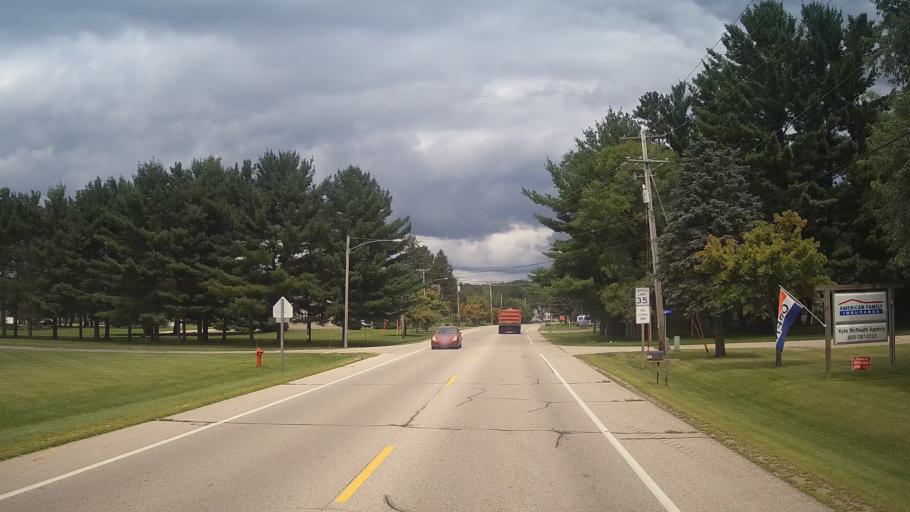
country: US
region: Wisconsin
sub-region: Waushara County
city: Wautoma
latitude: 44.0730
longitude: -89.2972
